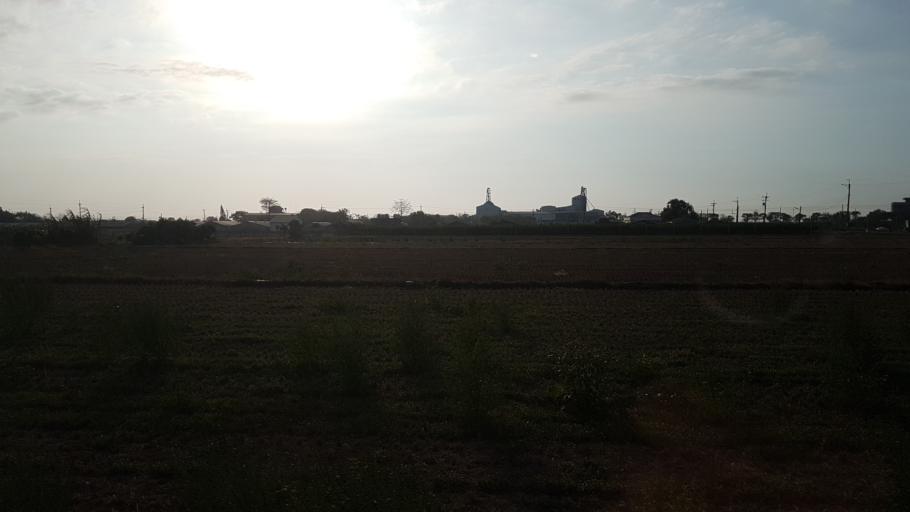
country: TW
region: Taiwan
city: Xinying
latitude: 23.3459
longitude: 120.3590
